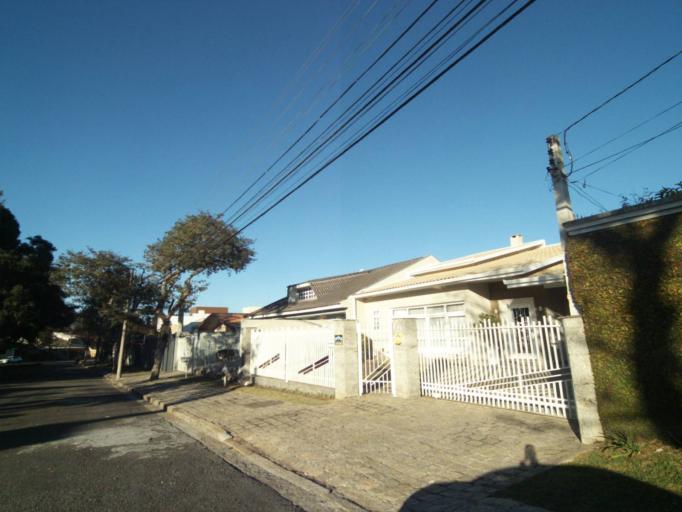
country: BR
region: Parana
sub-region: Pinhais
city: Pinhais
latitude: -25.4201
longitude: -49.2279
